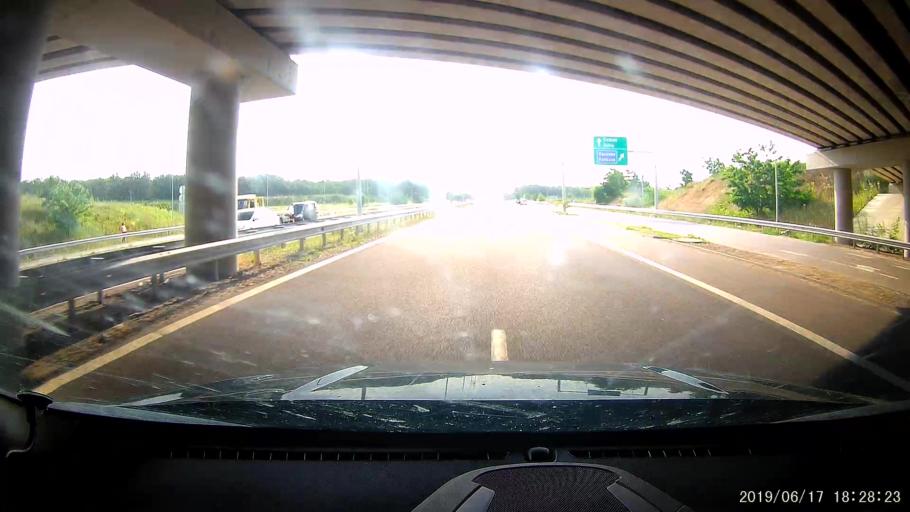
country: BG
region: Khaskovo
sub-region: Obshtina Dimitrovgrad
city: Dimitrovgrad
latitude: 42.0224
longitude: 25.5811
